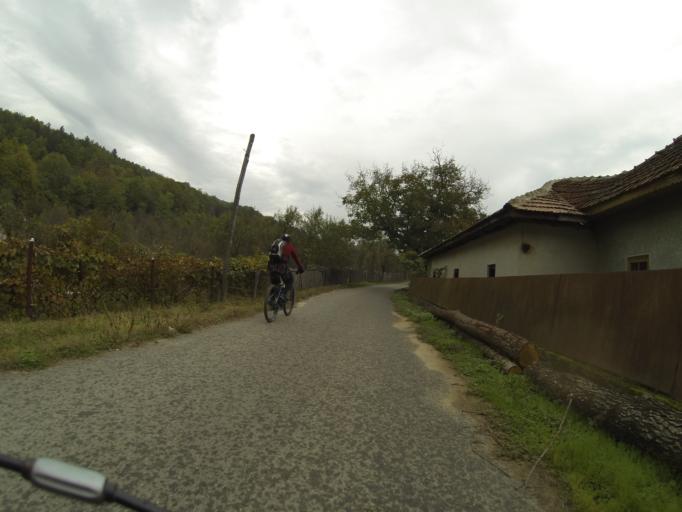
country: RO
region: Gorj
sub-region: Comuna Tismana
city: Pocruia
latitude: 45.0495
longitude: 22.9181
